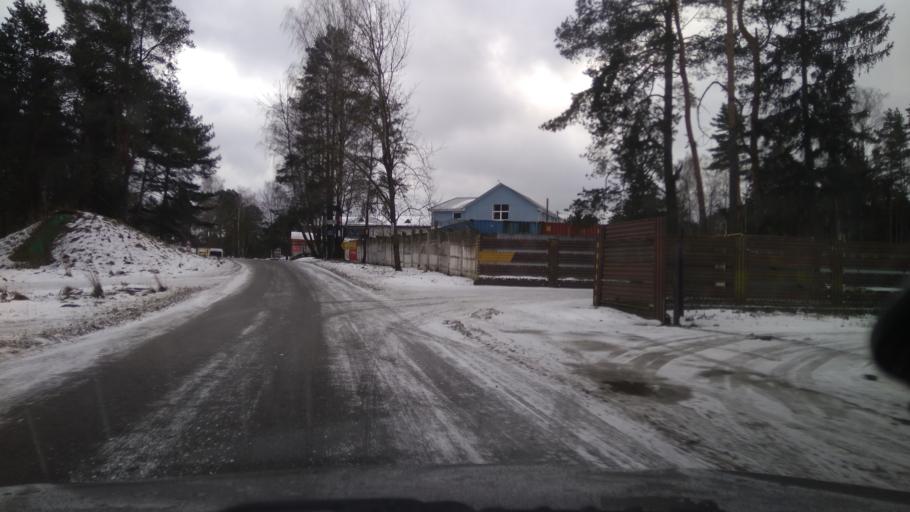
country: BY
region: Minsk
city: Borovlyany
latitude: 53.9625
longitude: 27.6479
